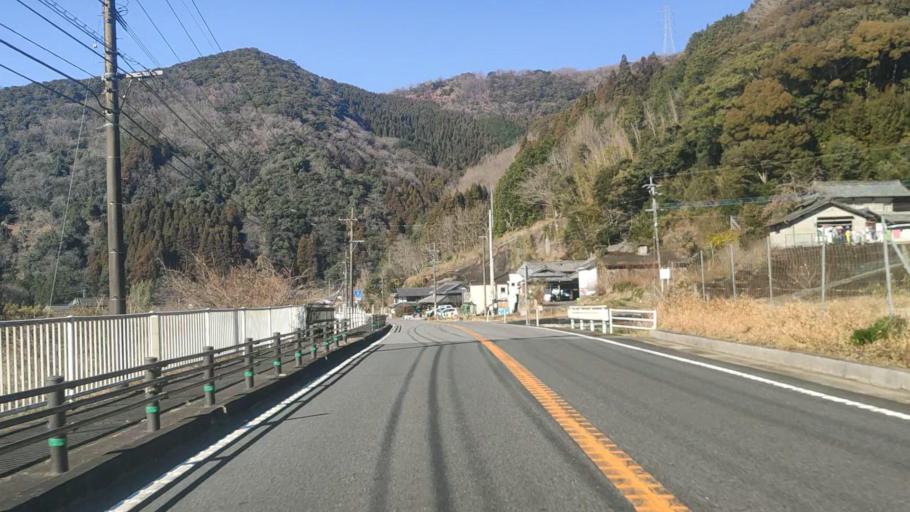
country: JP
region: Oita
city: Usuki
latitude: 33.0046
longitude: 131.7422
